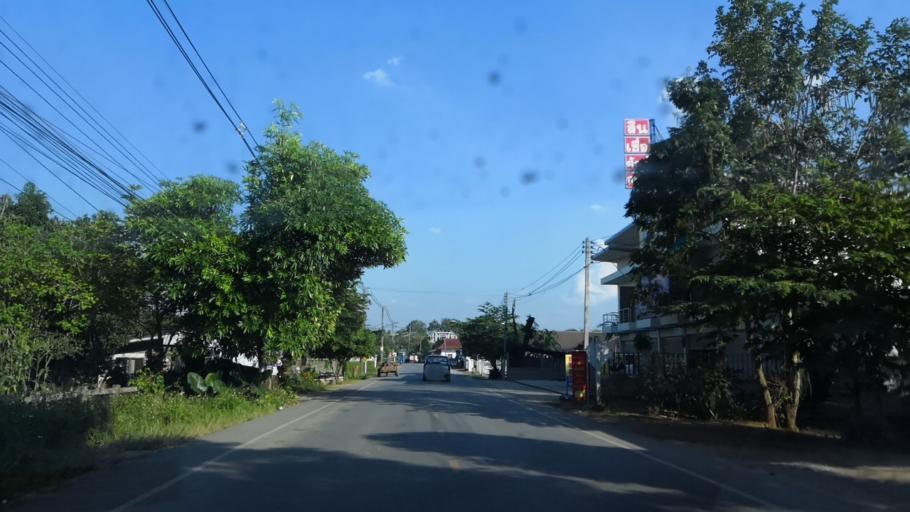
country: TH
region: Chiang Rai
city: Wiang Chai
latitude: 19.9324
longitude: 99.8947
